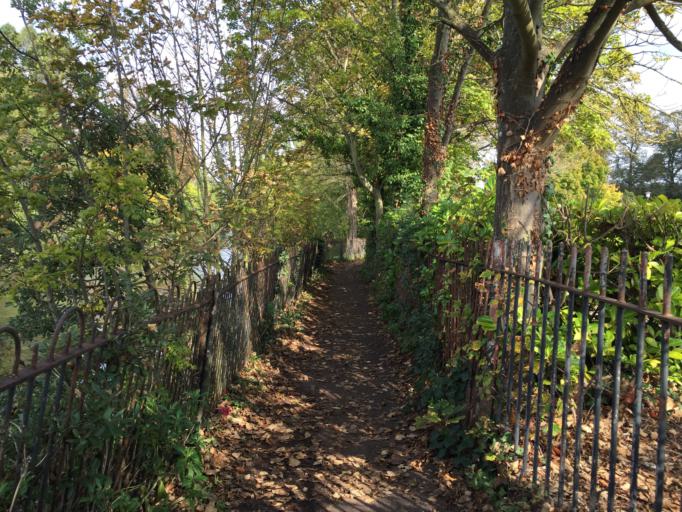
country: GB
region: England
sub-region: West Berkshire
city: Eton
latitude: 51.4871
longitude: -0.6061
